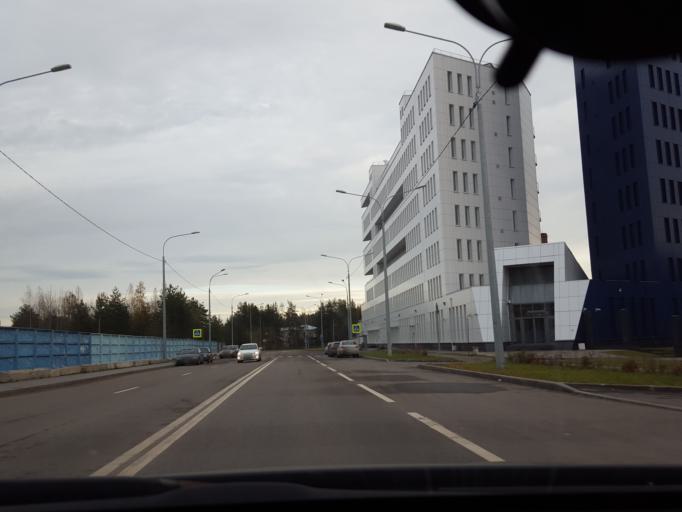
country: RU
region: St.-Petersburg
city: Pargolovo
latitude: 60.0482
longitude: 30.2422
